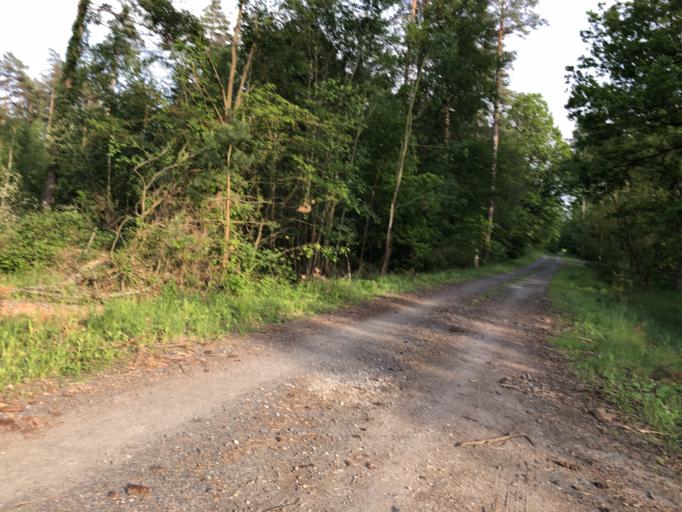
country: DE
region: Bavaria
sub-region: Upper Franconia
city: Memmelsdorf
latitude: 49.9069
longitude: 10.9586
